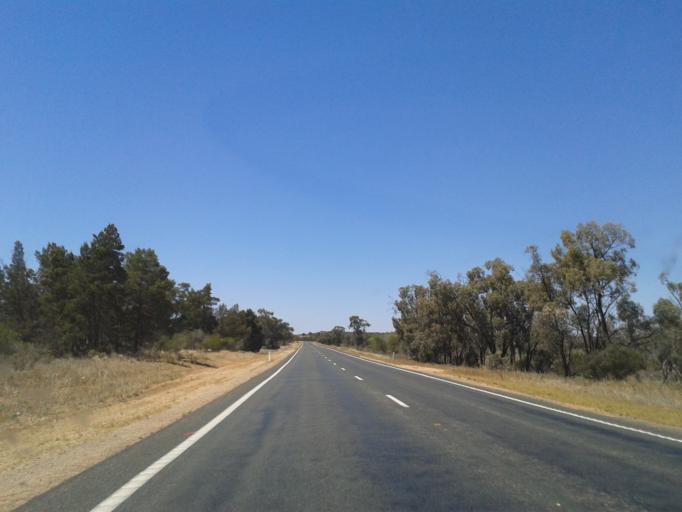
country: AU
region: New South Wales
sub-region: Wentworth
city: Gol Gol
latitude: -34.2909
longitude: 142.3123
